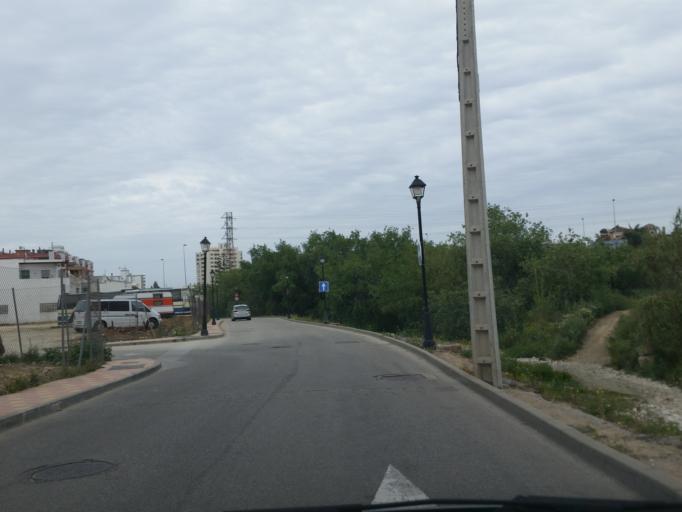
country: ES
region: Andalusia
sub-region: Provincia de Malaga
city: Fuengirola
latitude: 36.5596
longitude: -4.6179
